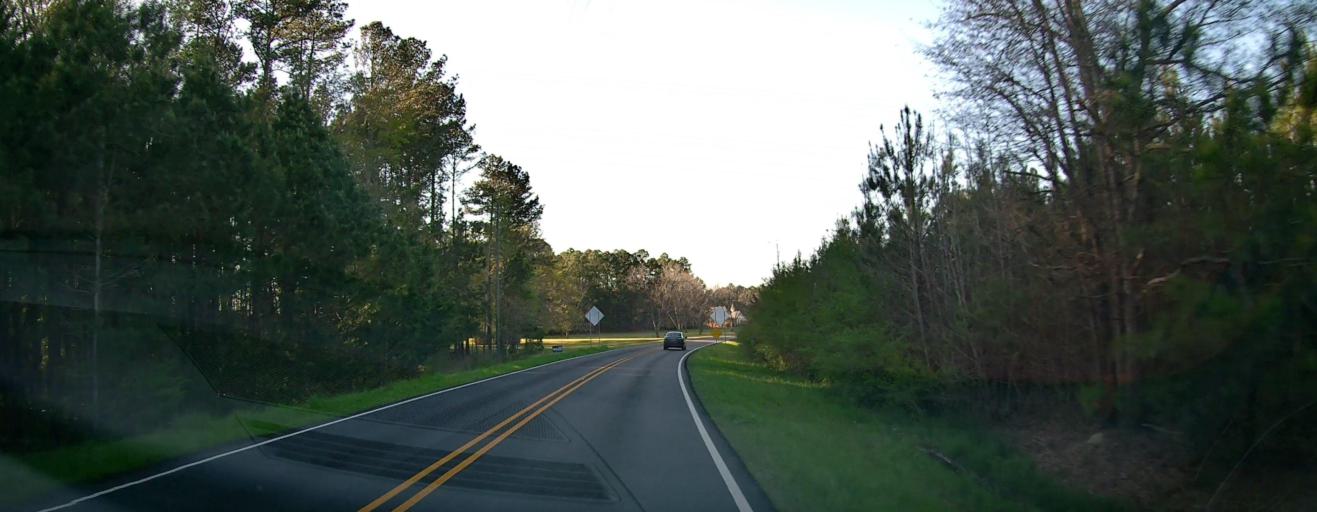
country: US
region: Georgia
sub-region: Butts County
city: Jackson
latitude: 33.3345
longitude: -83.9094
